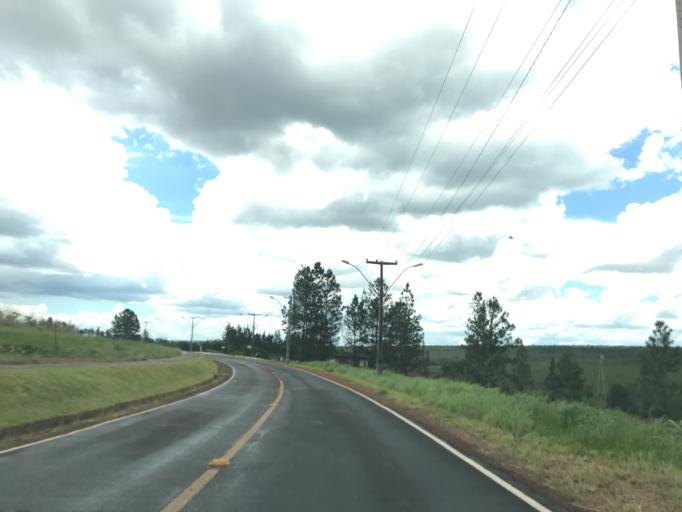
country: BR
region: Federal District
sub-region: Brasilia
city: Brasilia
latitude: -15.9007
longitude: -47.9144
